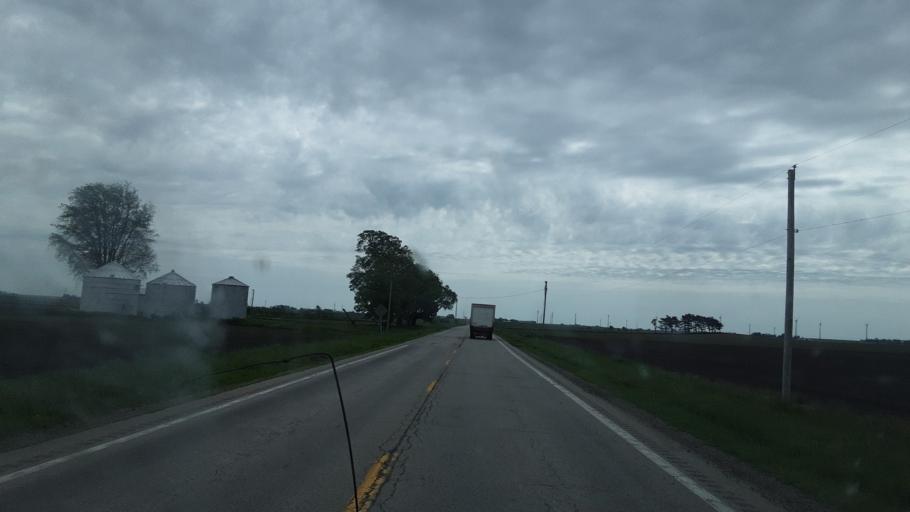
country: US
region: Illinois
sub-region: Tazewell County
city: Delavan
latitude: 40.3078
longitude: -89.4694
